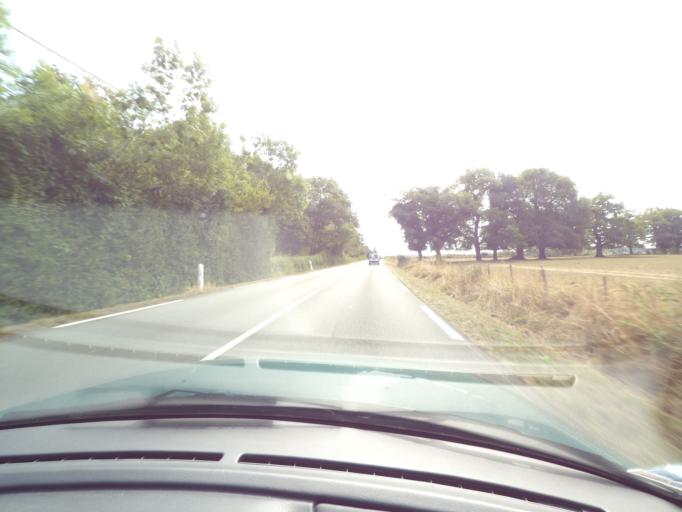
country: FR
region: Limousin
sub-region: Departement de la Haute-Vienne
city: Feytiat
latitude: 45.8047
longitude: 1.3716
